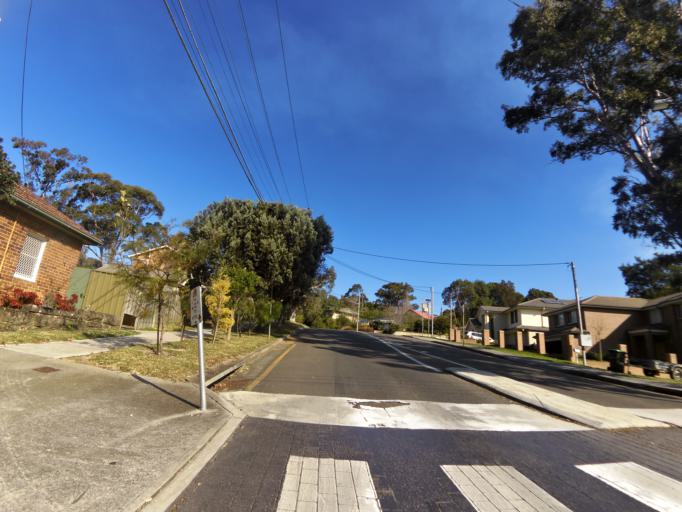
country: AU
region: New South Wales
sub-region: Sutherland Shire
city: Como
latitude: -34.0024
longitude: 151.0683
